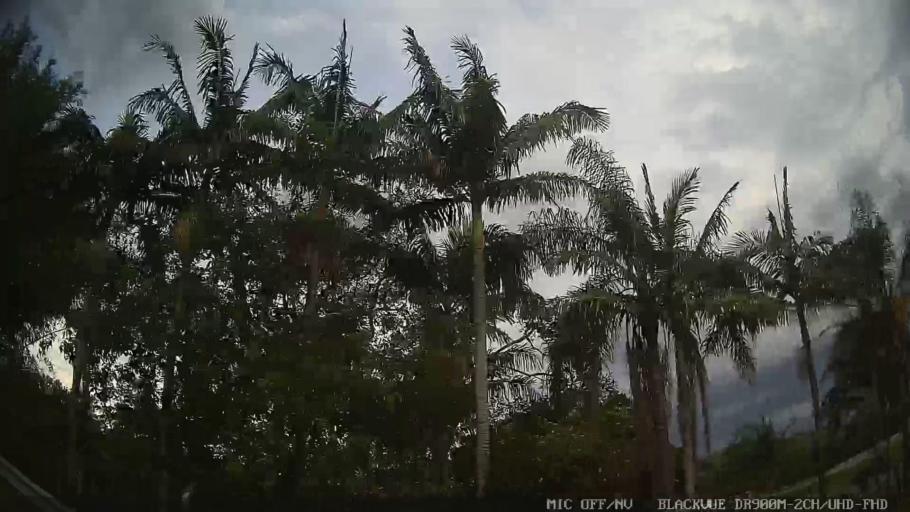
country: BR
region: Sao Paulo
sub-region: Amparo
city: Amparo
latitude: -22.8524
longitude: -46.7842
